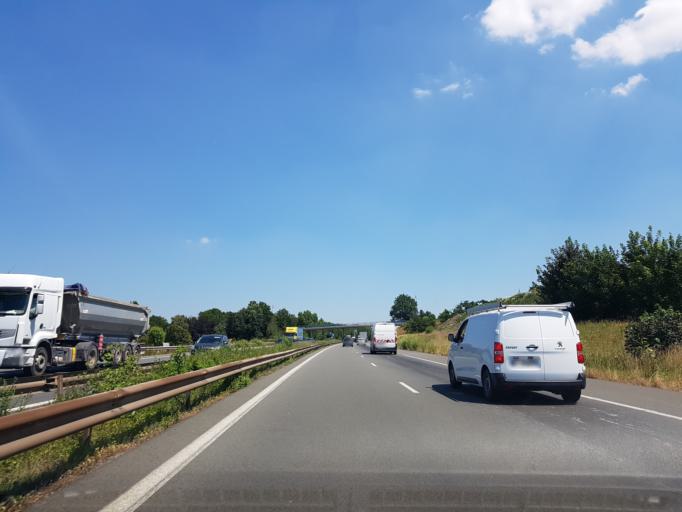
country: FR
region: Nord-Pas-de-Calais
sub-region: Departement du Nord
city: Lieu-Saint-Amand
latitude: 50.2756
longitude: 3.3379
